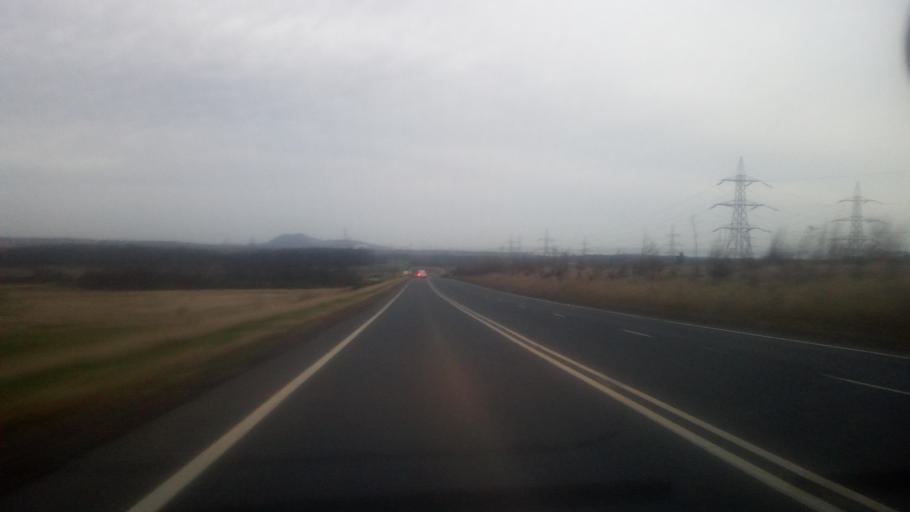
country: GB
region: Scotland
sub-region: Midlothian
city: Dalkeith
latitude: 55.9058
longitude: -3.0355
